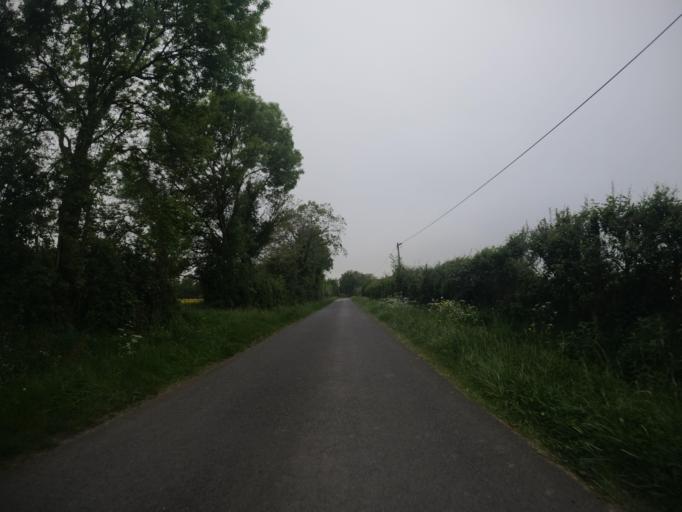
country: FR
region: Poitou-Charentes
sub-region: Departement des Deux-Sevres
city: Chiche
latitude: 46.8676
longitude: -0.3379
